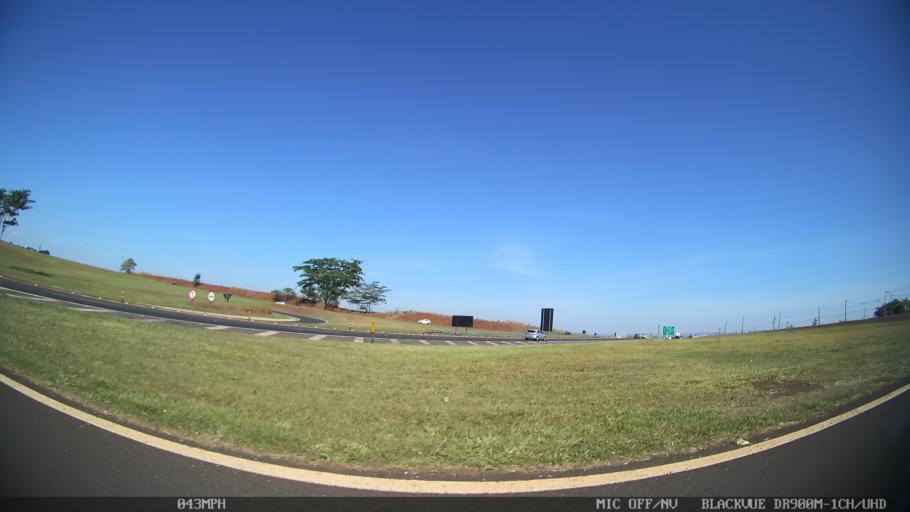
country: BR
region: Sao Paulo
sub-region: Jardinopolis
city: Jardinopolis
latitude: -21.0934
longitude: -47.7953
